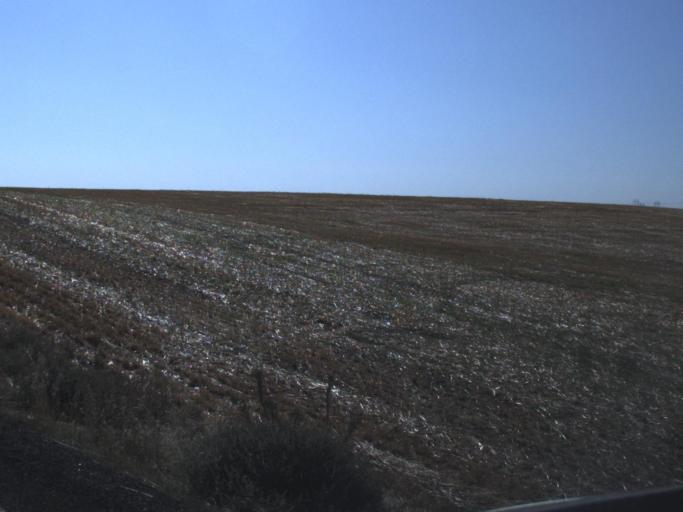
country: US
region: Washington
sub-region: Walla Walla County
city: Walla Walla
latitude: 46.0904
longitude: -118.3674
